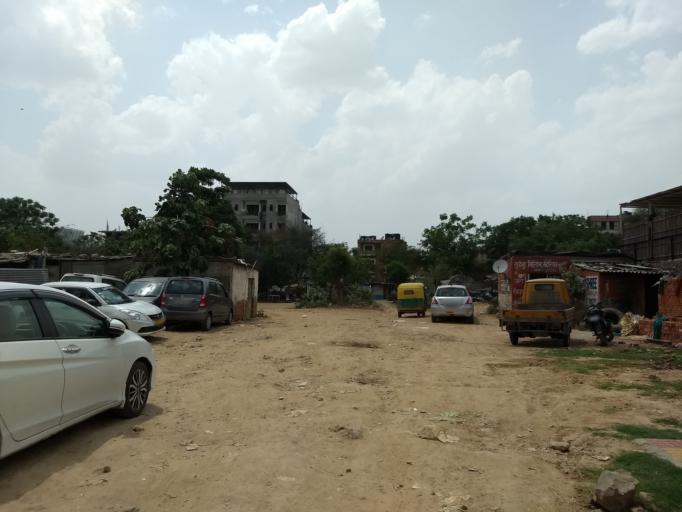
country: IN
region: Haryana
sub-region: Gurgaon
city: Gurgaon
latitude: 28.4955
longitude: 77.1021
